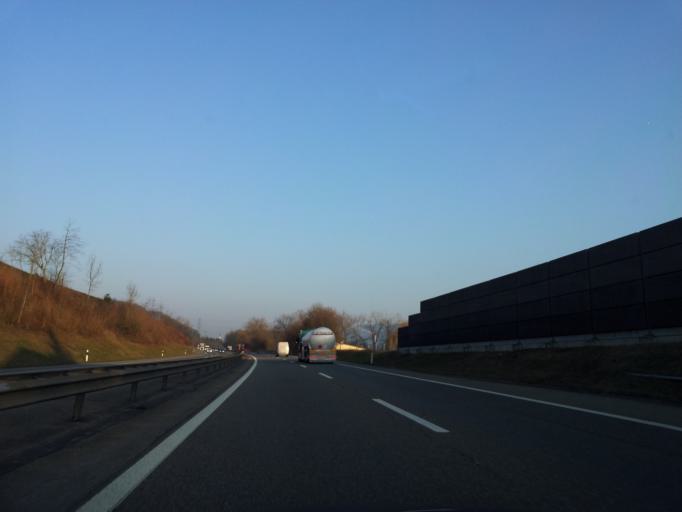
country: CH
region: Aargau
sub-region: Bezirk Laufenburg
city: Frick
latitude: 47.5194
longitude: 8.0123
